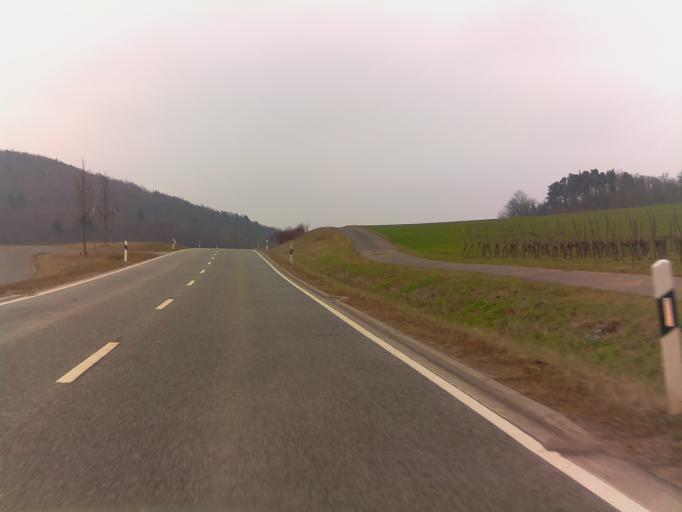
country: DE
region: Rheinland-Pfalz
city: Frei-Laubersheim
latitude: 49.7938
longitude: 7.8942
